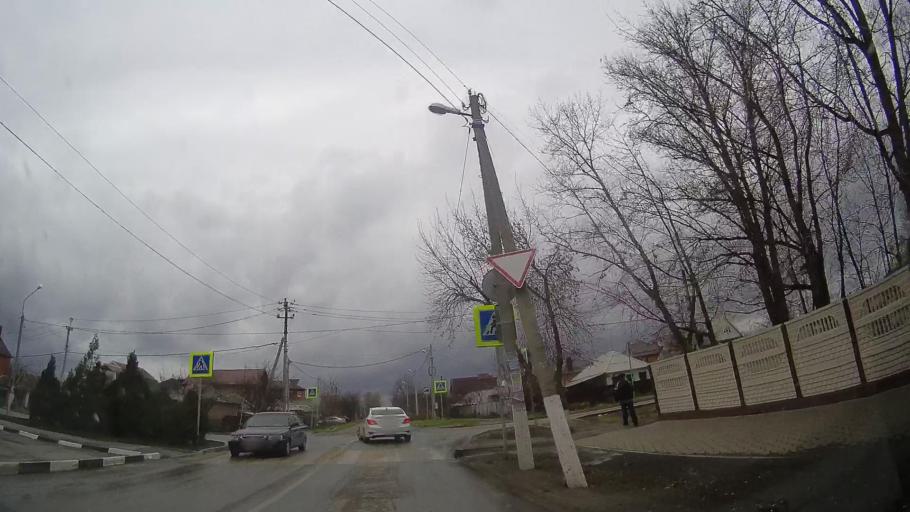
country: RU
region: Rostov
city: Bataysk
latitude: 47.1150
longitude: 39.7440
